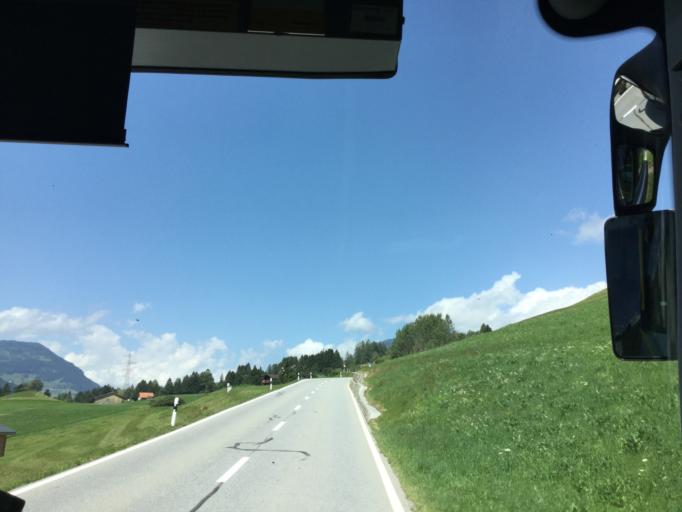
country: CH
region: Grisons
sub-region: Albula District
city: Tiefencastel
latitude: 46.6679
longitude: 9.5823
